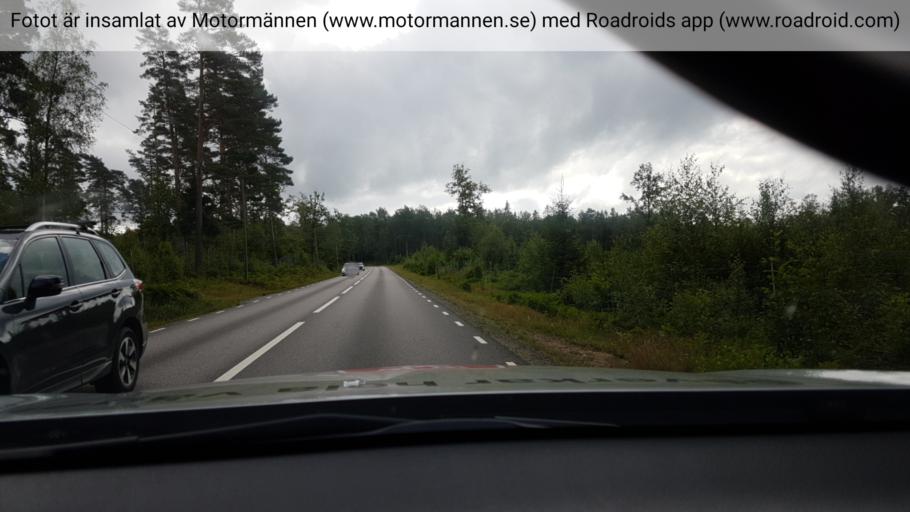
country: SE
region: Vaestra Goetaland
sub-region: Marks Kommun
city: Kinna
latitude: 57.4693
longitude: 12.7376
